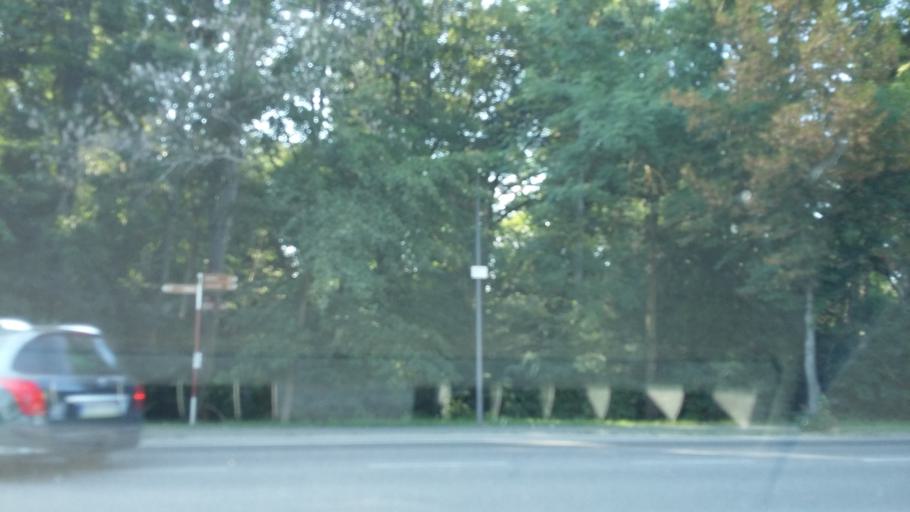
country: CZ
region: Central Bohemia
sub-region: Okres Nymburk
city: Podebrady
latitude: 50.1386
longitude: 15.1125
